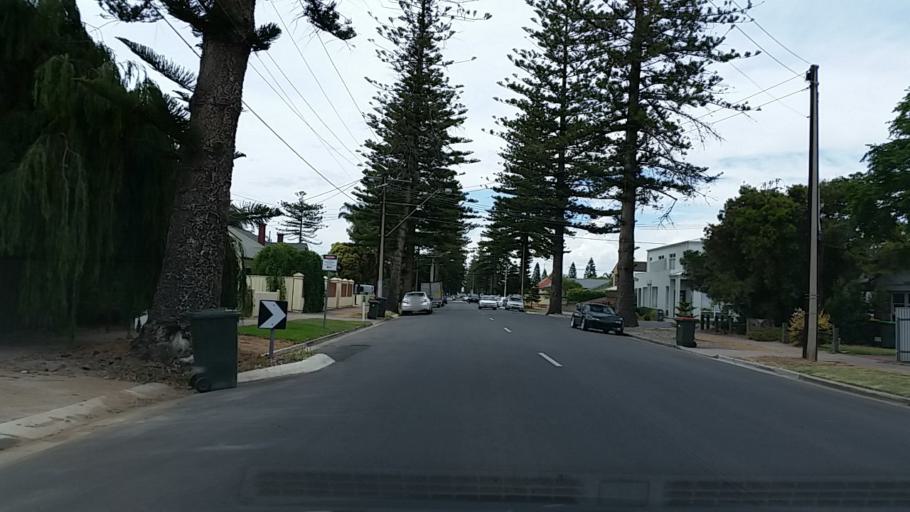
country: AU
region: South Australia
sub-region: Adelaide
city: Glenelg
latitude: -34.9746
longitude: 138.5173
